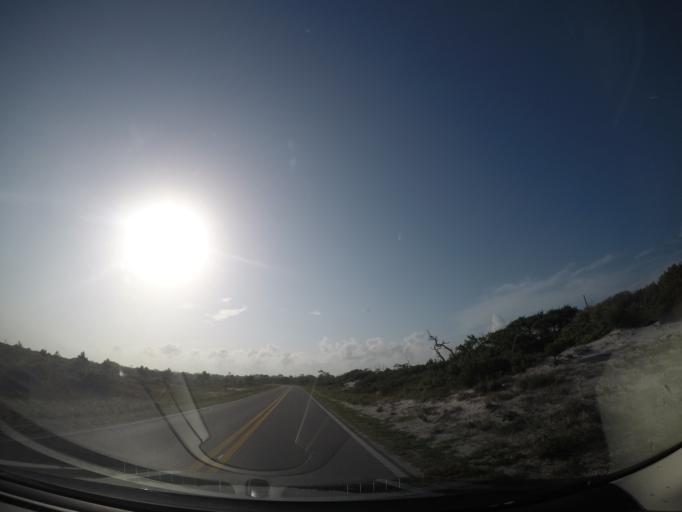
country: US
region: Florida
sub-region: Escambia County
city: Warrington
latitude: 30.3198
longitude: -87.2727
